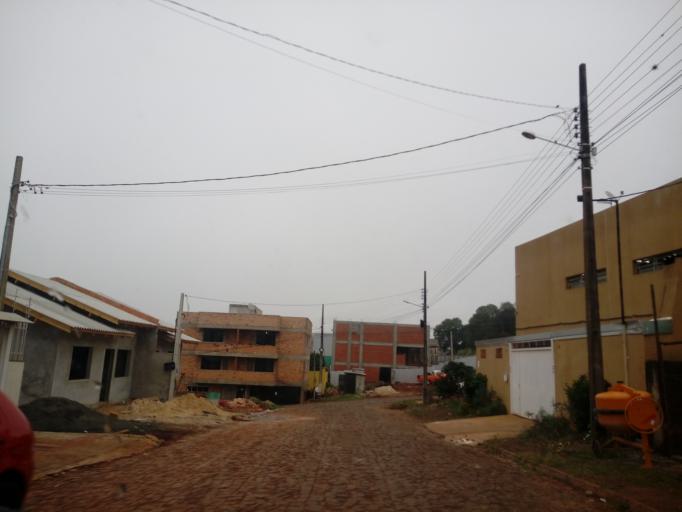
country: BR
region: Santa Catarina
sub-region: Chapeco
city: Chapeco
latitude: -27.1018
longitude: -52.6731
